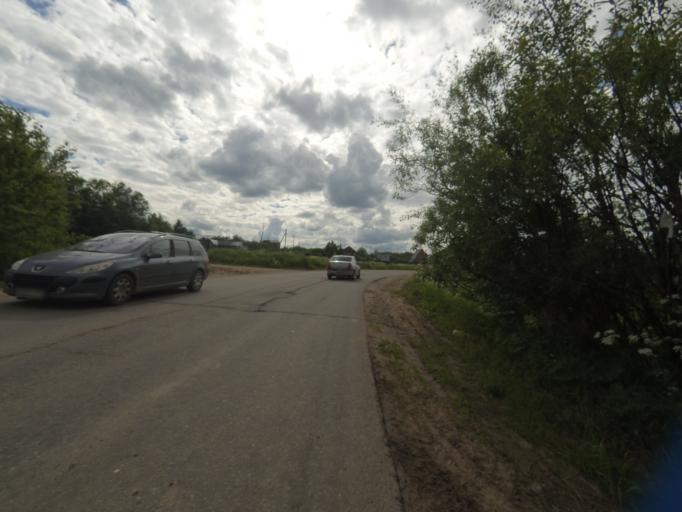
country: RU
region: Moskovskaya
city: Marfino
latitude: 56.0785
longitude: 37.5954
